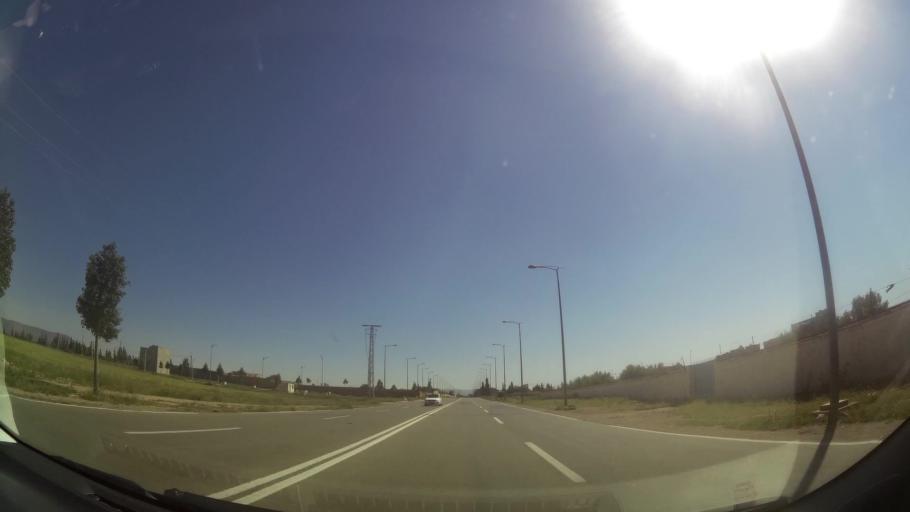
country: MA
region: Oriental
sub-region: Oujda-Angad
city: Oujda
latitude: 34.7250
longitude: -1.8779
